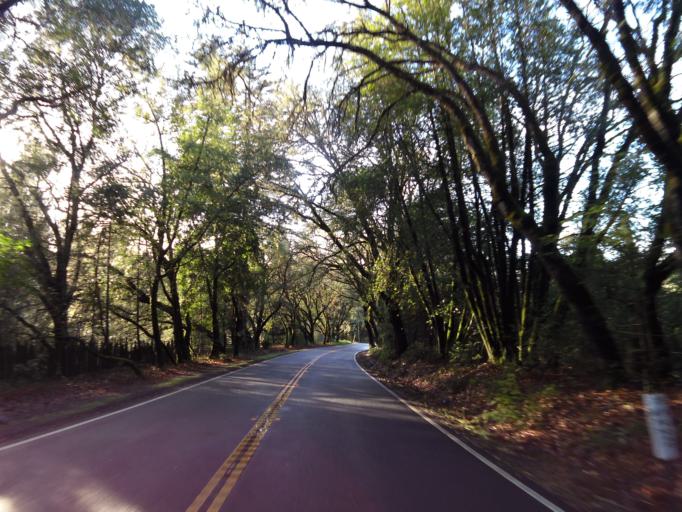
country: US
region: California
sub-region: Mendocino County
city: Boonville
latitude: 39.0672
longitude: -123.4493
